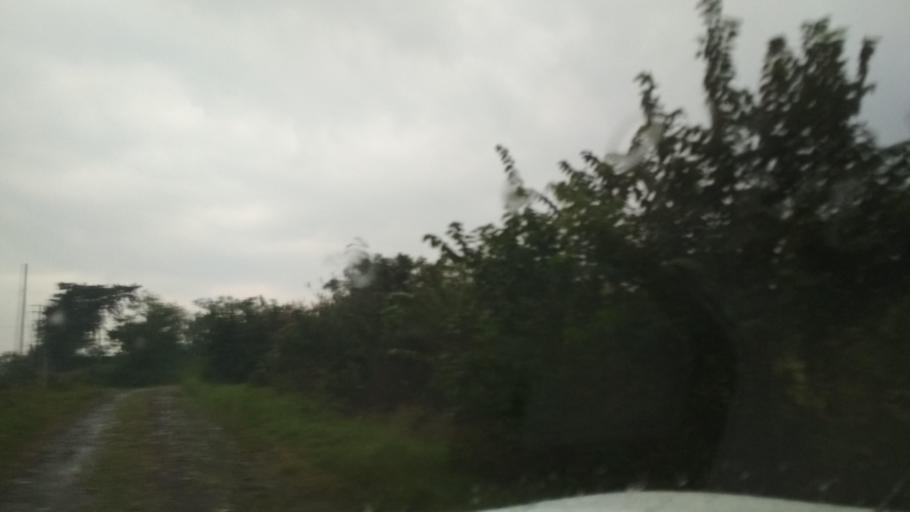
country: MM
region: Shan
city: Taunggyi
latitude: 20.3017
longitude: 97.3036
